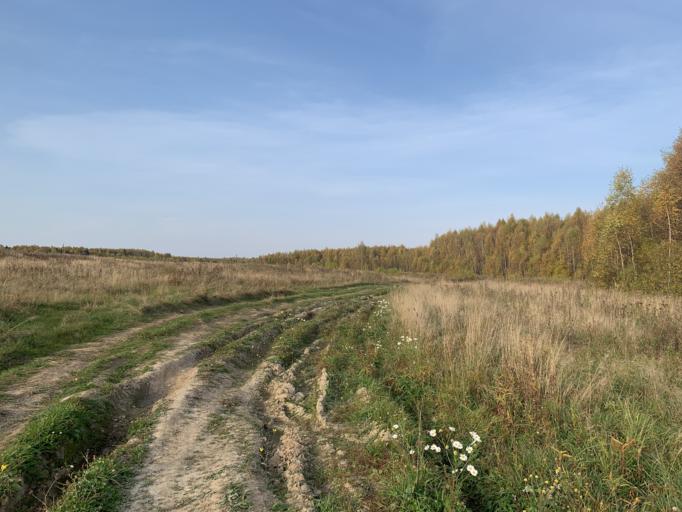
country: RU
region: Jaroslavl
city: Porech'ye-Rybnoye
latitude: 56.9834
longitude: 39.3838
